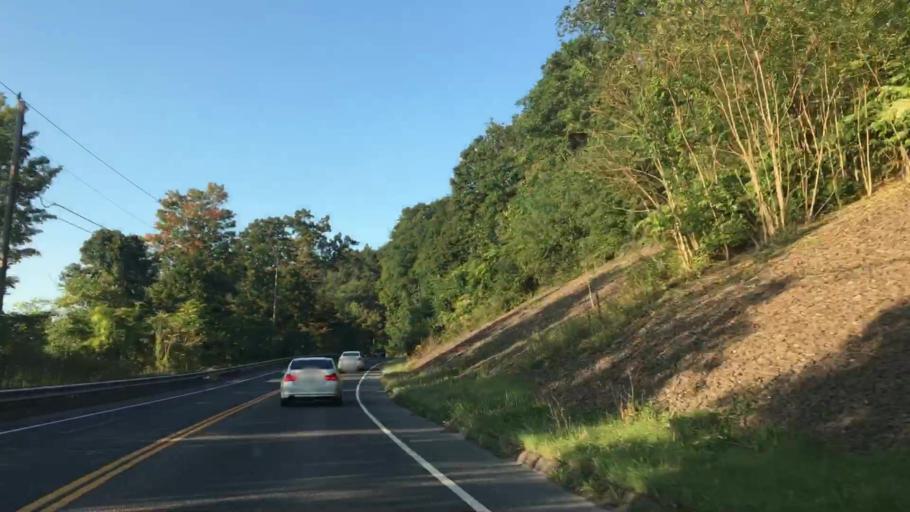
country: US
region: Connecticut
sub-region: Litchfield County
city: New Milford
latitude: 41.5599
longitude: -73.4051
